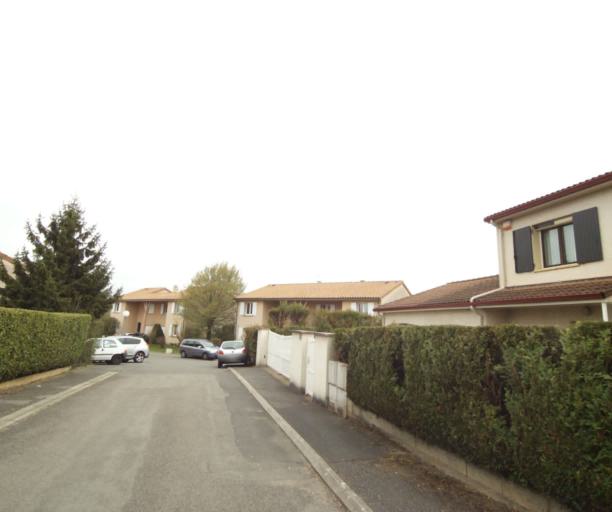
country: FR
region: Bourgogne
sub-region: Departement de Saone-et-Loire
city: Charnay-les-Macon
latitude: 46.3050
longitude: 4.7990
